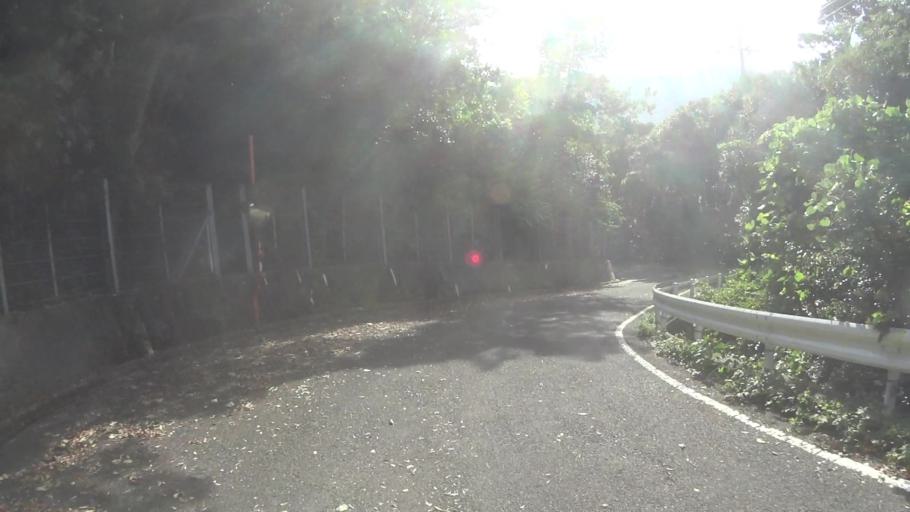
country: JP
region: Kyoto
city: Maizuru
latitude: 35.5614
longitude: 135.4045
